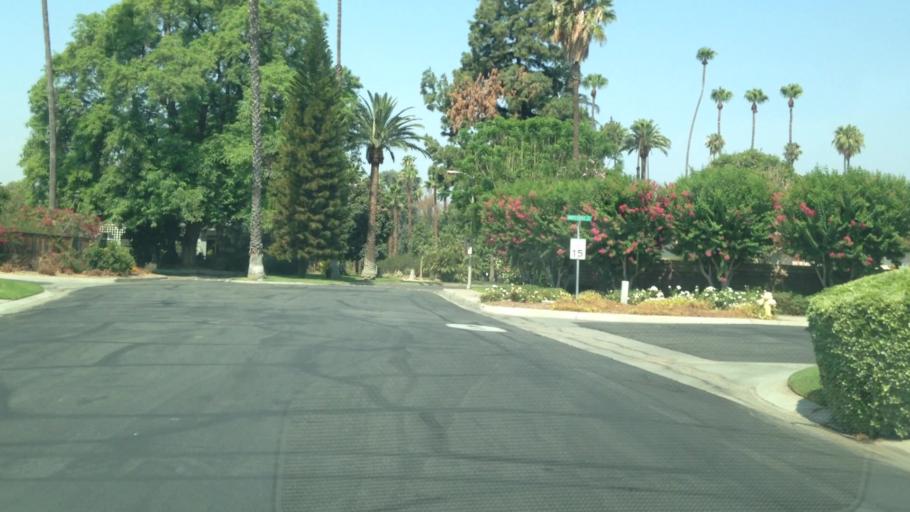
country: US
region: California
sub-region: Riverside County
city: Riverside
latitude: 33.9338
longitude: -117.3803
